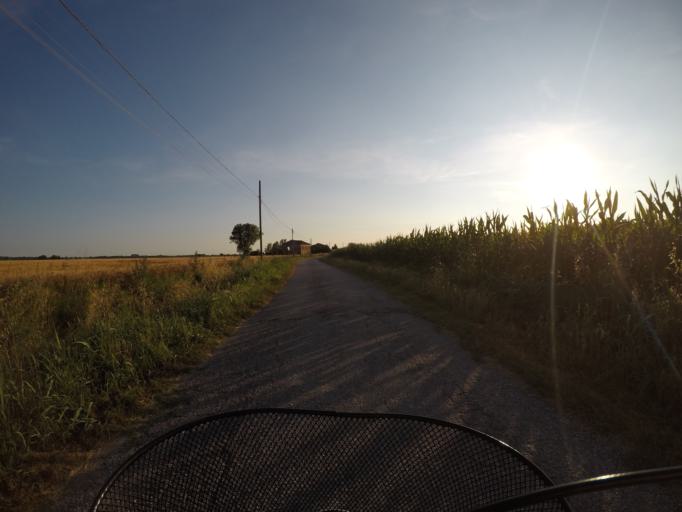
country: IT
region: Veneto
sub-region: Provincia di Rovigo
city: San Bellino
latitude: 45.0177
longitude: 11.6065
